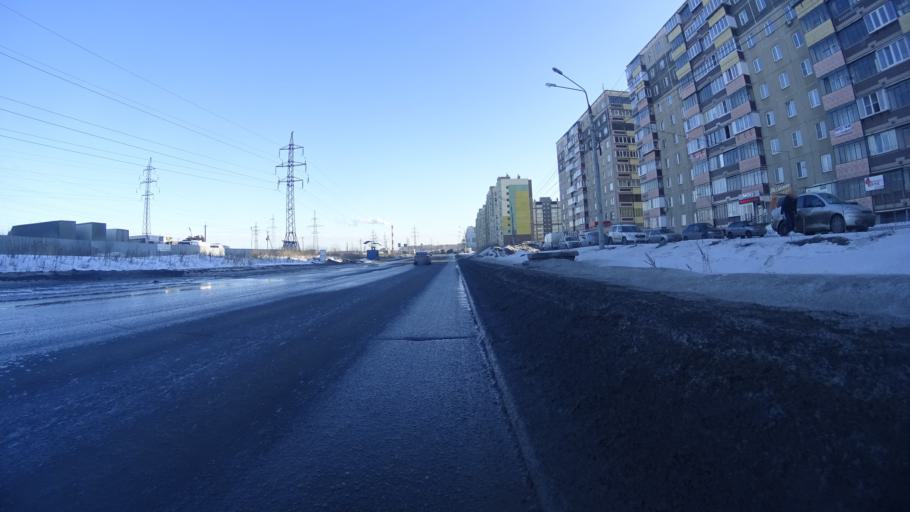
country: RU
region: Chelyabinsk
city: Roshchino
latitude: 55.2195
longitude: 61.2980
